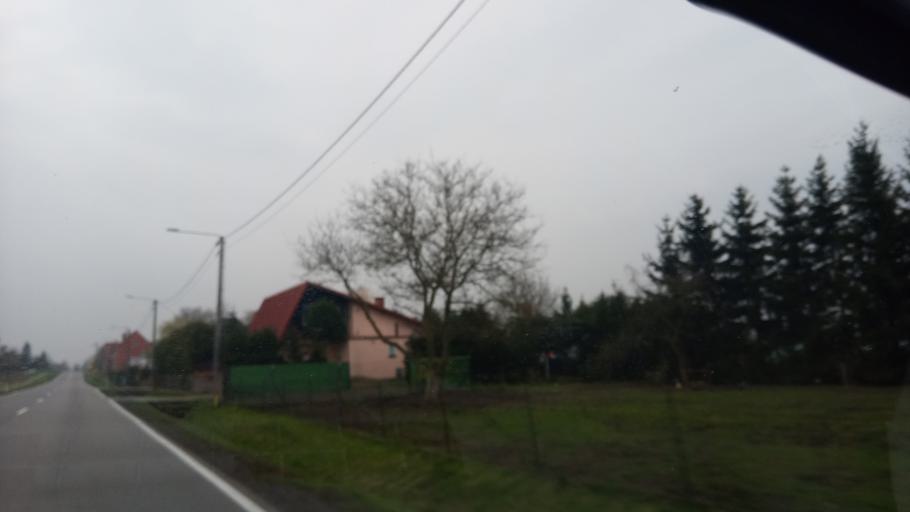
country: PL
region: Pomeranian Voivodeship
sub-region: Powiat czluchowski
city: Czluchow
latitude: 53.6815
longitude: 17.3361
